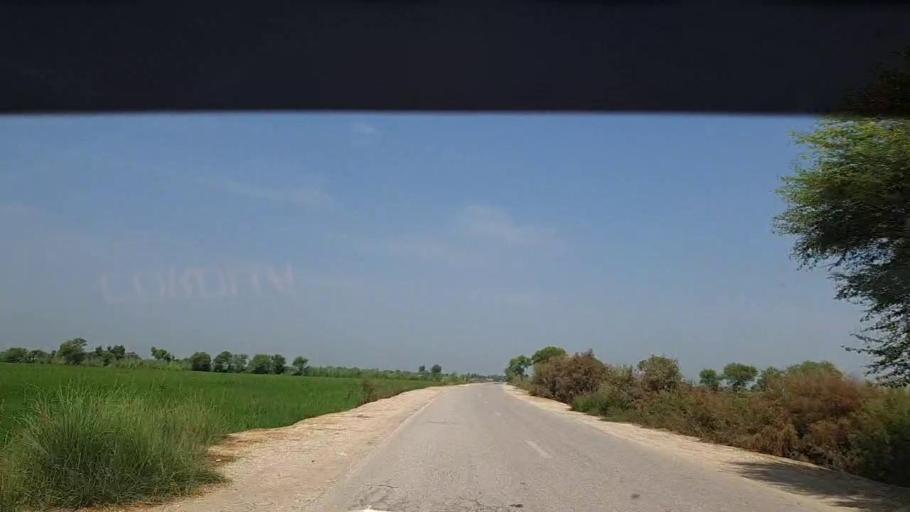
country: PK
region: Sindh
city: Thul
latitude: 28.1339
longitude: 68.8176
